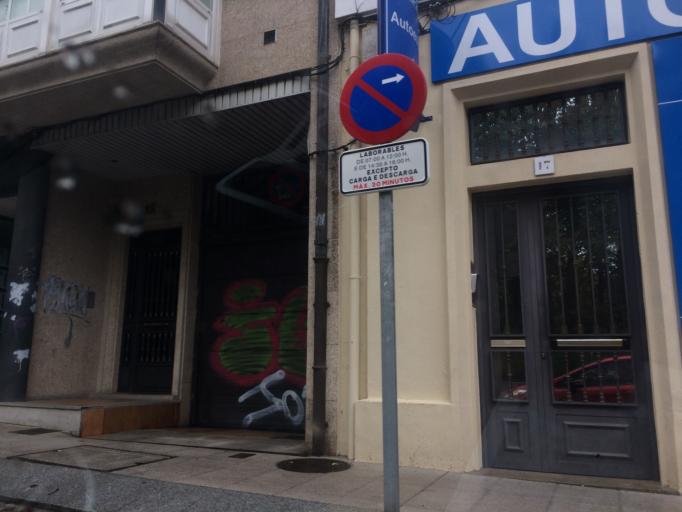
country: ES
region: Galicia
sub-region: Provincia da Coruna
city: Santiago de Compostela
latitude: 42.8749
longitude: -8.5525
